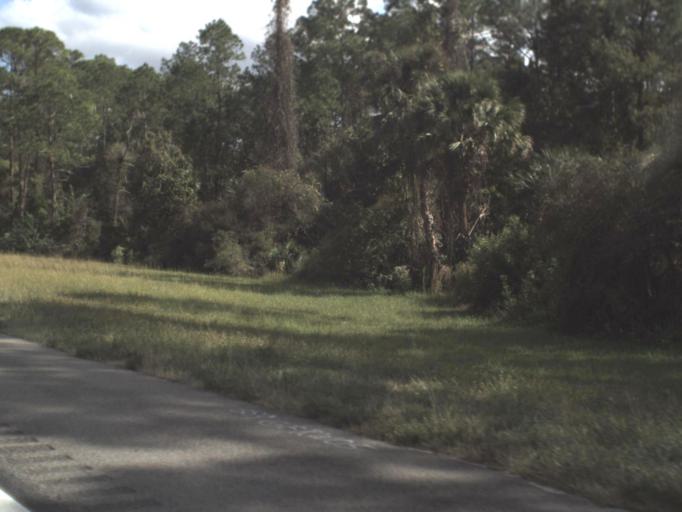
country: US
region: Florida
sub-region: Orange County
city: Christmas
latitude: 28.4525
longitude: -80.9613
